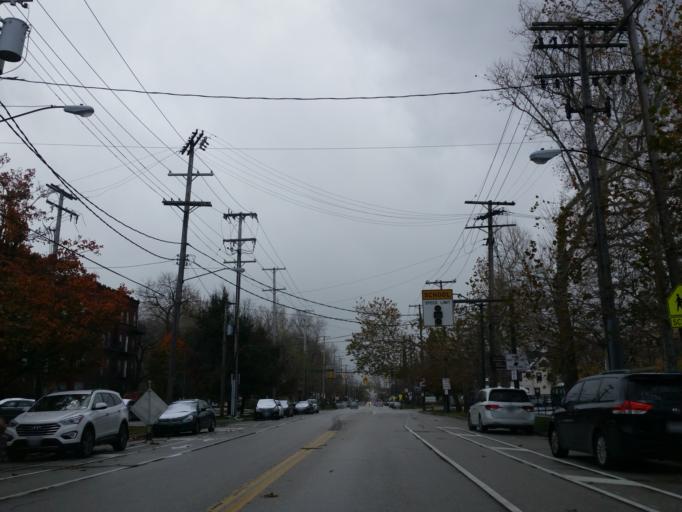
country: US
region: Ohio
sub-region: Cuyahoga County
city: Cleveland
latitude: 41.4808
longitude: -81.6914
